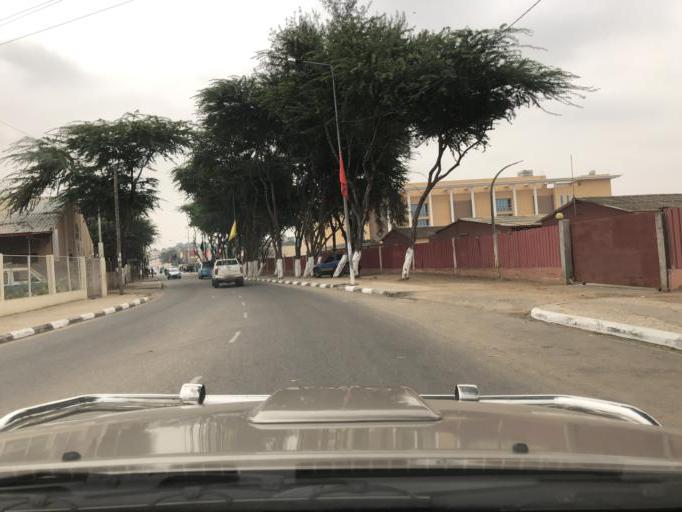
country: AO
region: Luanda
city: Luanda
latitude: -8.9083
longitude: 13.1631
